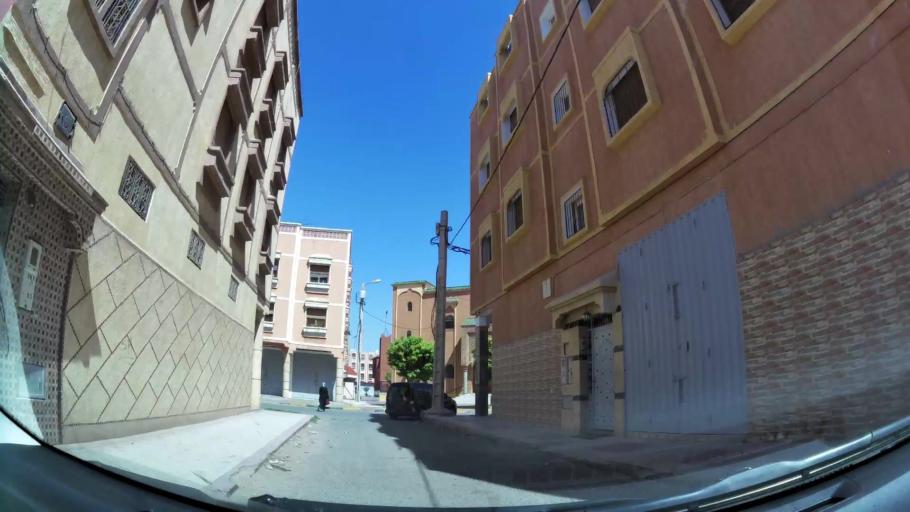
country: MA
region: Souss-Massa-Draa
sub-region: Inezgane-Ait Mellou
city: Inezgane
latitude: 30.3318
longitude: -9.5056
